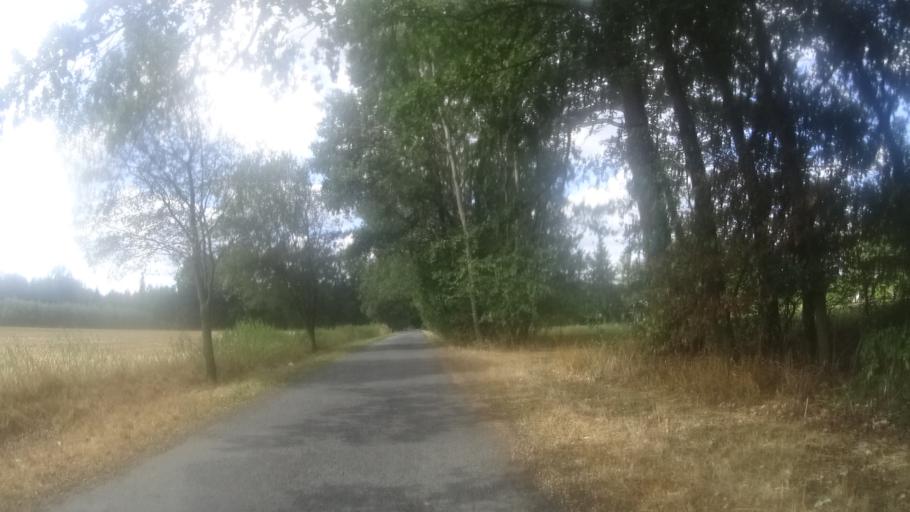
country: CZ
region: Pardubicky
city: Horni Jeleni
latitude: 50.0461
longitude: 16.1580
